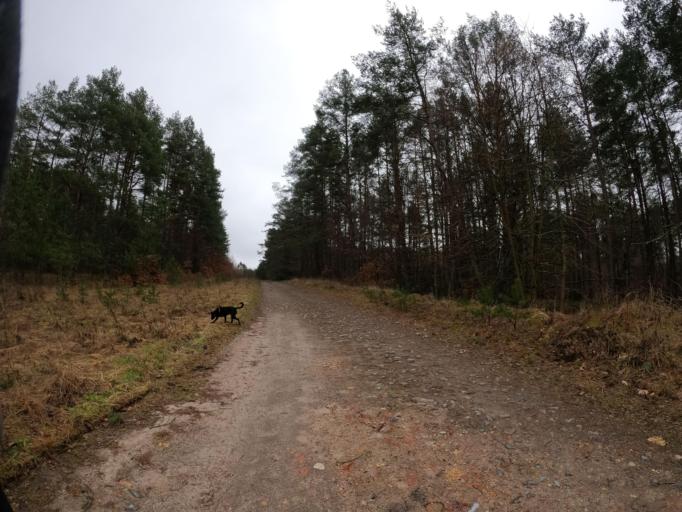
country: PL
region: Greater Poland Voivodeship
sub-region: Powiat zlotowski
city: Sypniewo
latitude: 53.4981
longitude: 16.5603
